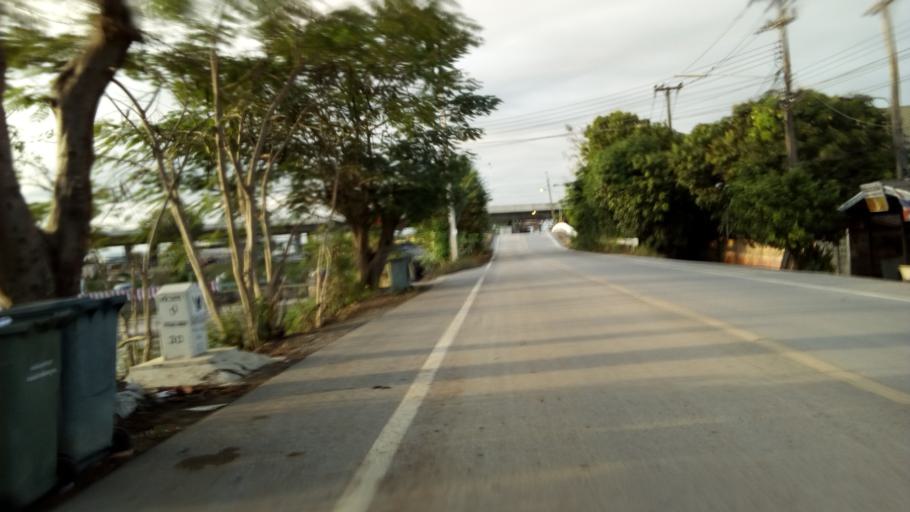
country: TH
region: Pathum Thani
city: Nong Suea
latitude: 14.0759
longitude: 100.8945
